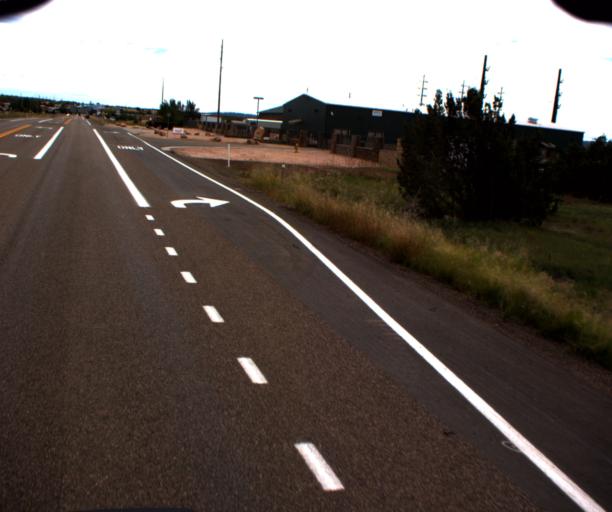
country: US
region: Arizona
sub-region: Navajo County
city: Show Low
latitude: 34.2619
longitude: -110.0199
